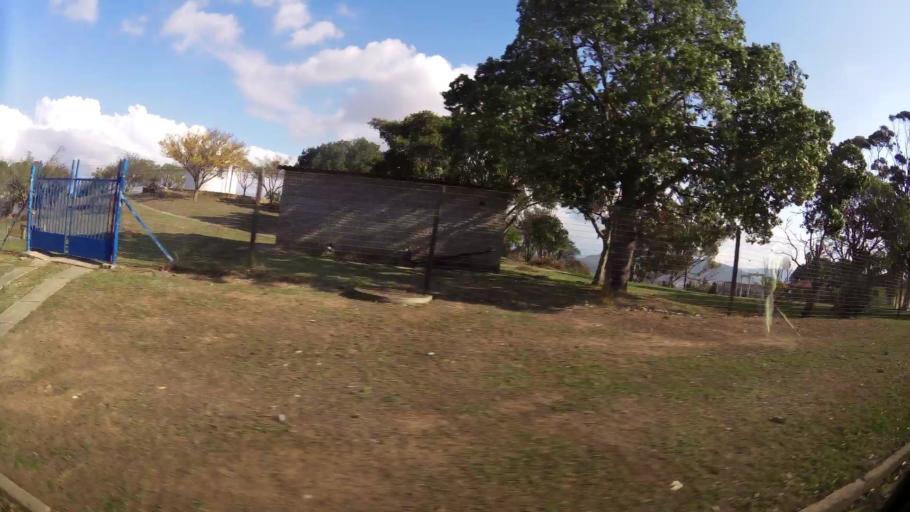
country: ZA
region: Eastern Cape
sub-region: Nelson Mandela Bay Metropolitan Municipality
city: Uitenhage
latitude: -33.7666
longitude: 25.4063
